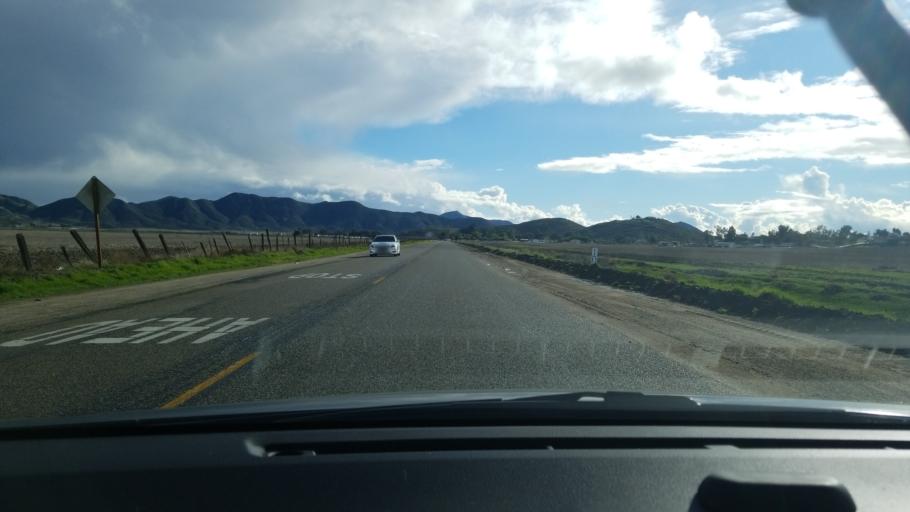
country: US
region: California
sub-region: Riverside County
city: Green Acres
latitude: 33.7278
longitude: -117.0502
